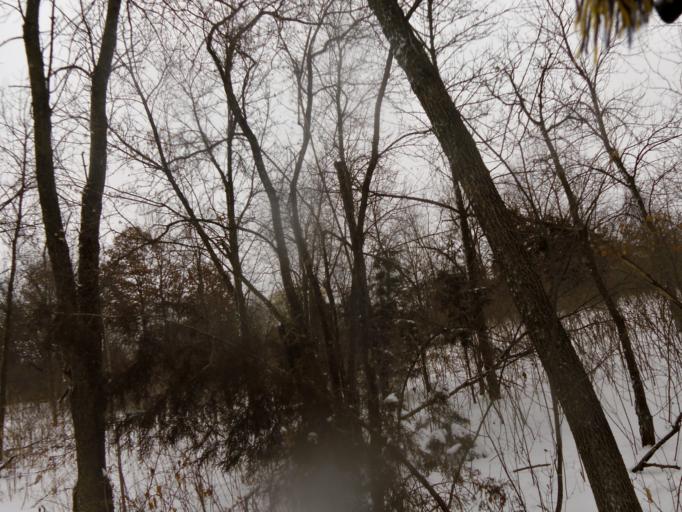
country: US
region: Minnesota
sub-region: Dakota County
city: Inver Grove Heights
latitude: 44.8657
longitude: -93.0748
